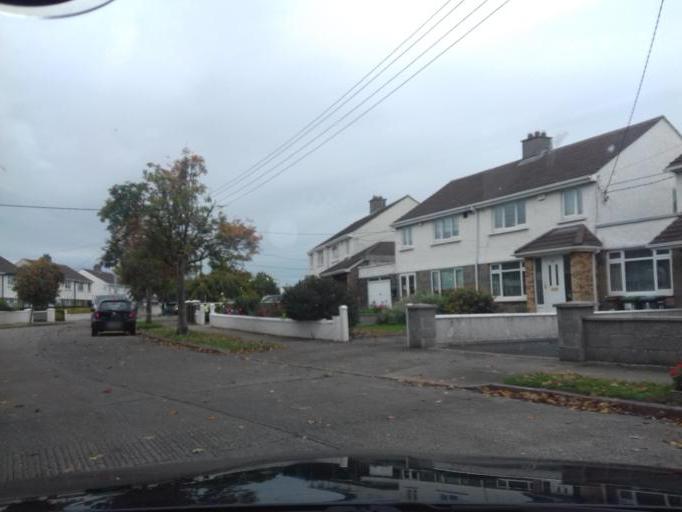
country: IE
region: Leinster
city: Beaumont
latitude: 53.3920
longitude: -6.2376
